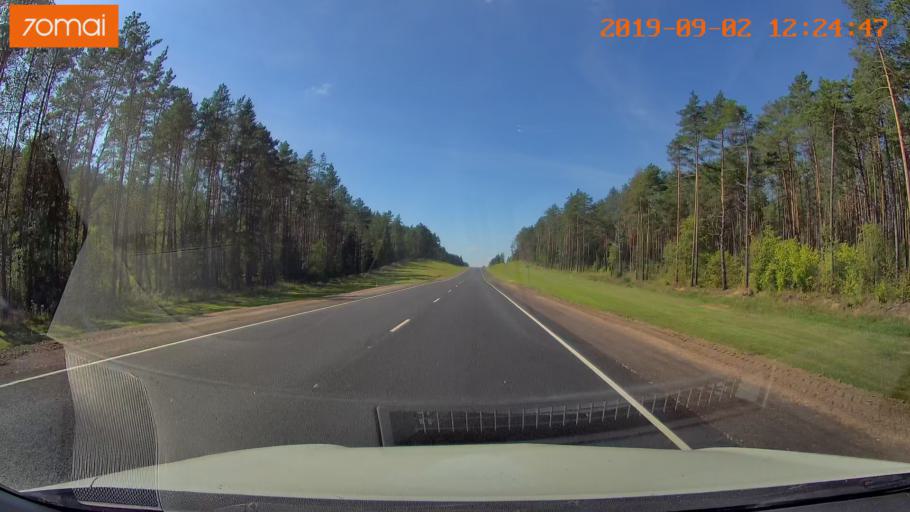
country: RU
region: Smolensk
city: Shumyachi
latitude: 53.8659
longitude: 32.5997
